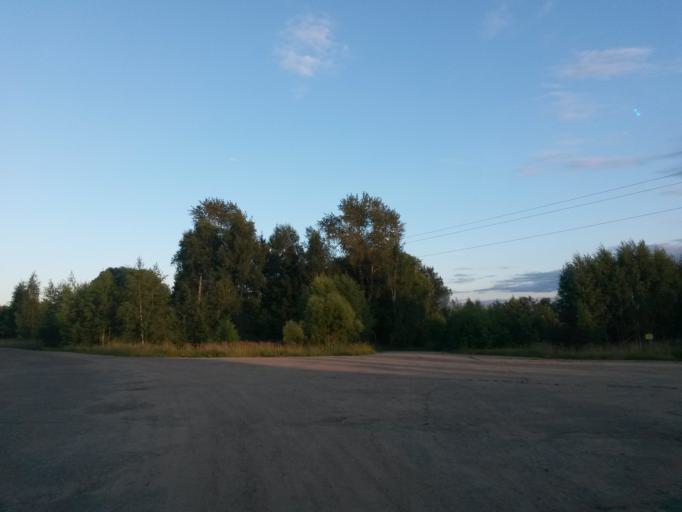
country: RU
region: Jaroslavl
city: Gavrilov-Yam
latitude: 57.3508
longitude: 40.0385
